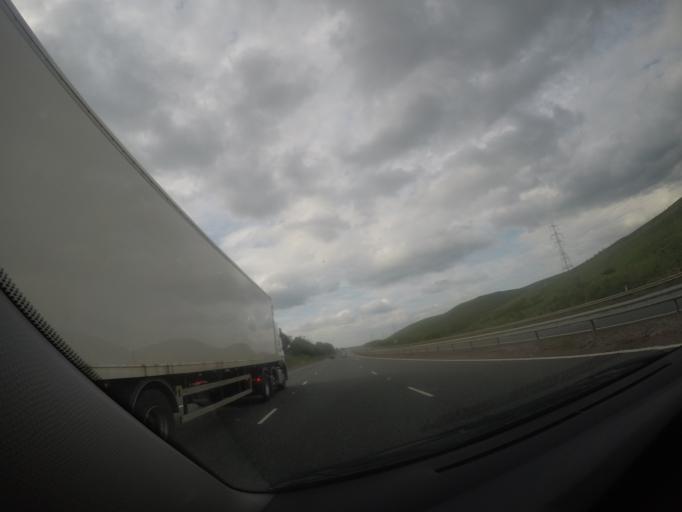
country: GB
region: Scotland
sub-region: South Lanarkshire
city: Douglas
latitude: 55.5514
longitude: -3.8008
